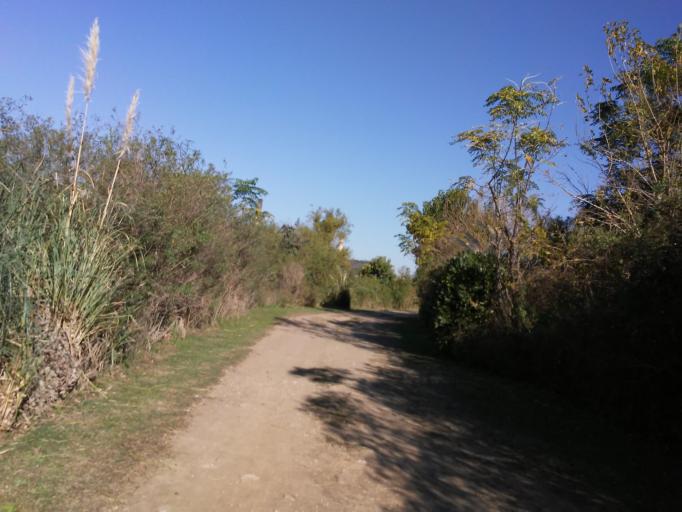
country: AR
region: Buenos Aires F.D.
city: Buenos Aires
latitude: -34.6156
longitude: -58.3401
